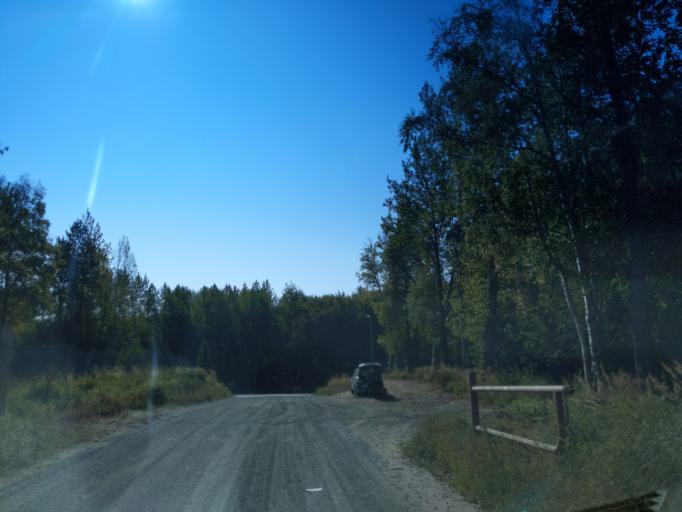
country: US
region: Alaska
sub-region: Anchorage Municipality
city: Anchorage
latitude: 61.1600
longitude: -150.0117
